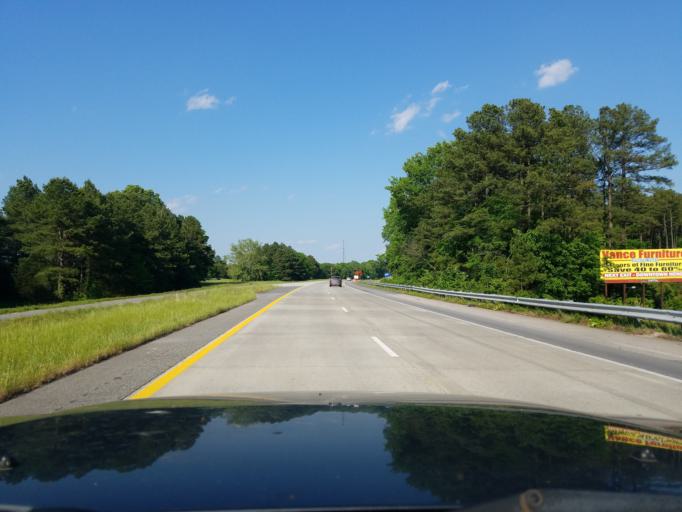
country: US
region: North Carolina
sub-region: Vance County
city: Henderson
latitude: 36.3373
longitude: -78.4315
